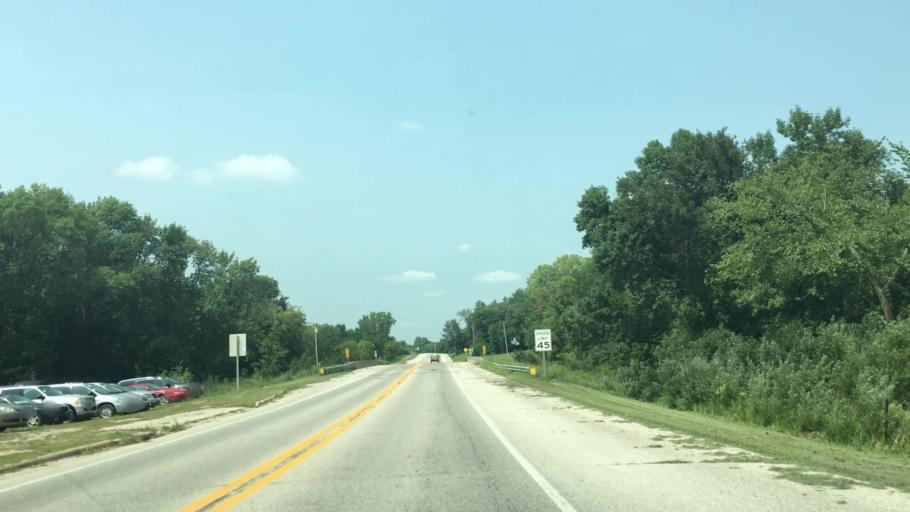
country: US
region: Iowa
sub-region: Fayette County
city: Oelwein
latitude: 42.6214
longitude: -91.9060
